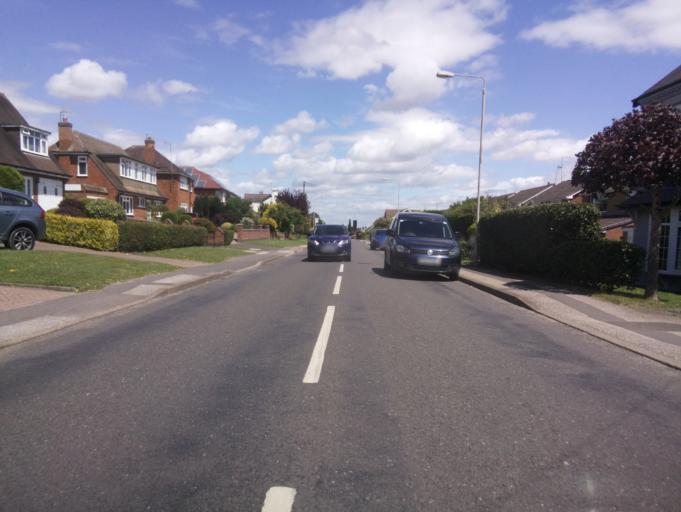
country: GB
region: England
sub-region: Nottinghamshire
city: Cotgrave
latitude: 52.8780
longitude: -1.0854
